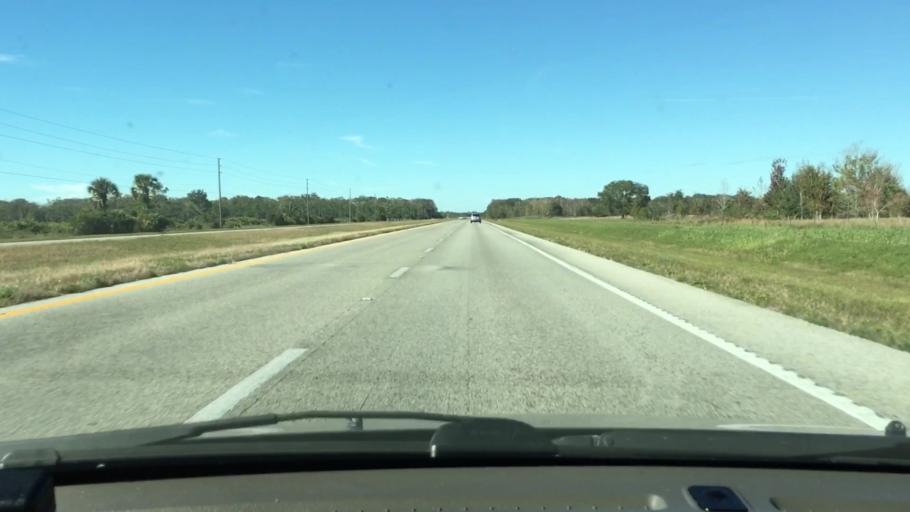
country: US
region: Florida
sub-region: Osceola County
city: Saint Cloud
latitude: 28.1292
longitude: -80.9920
